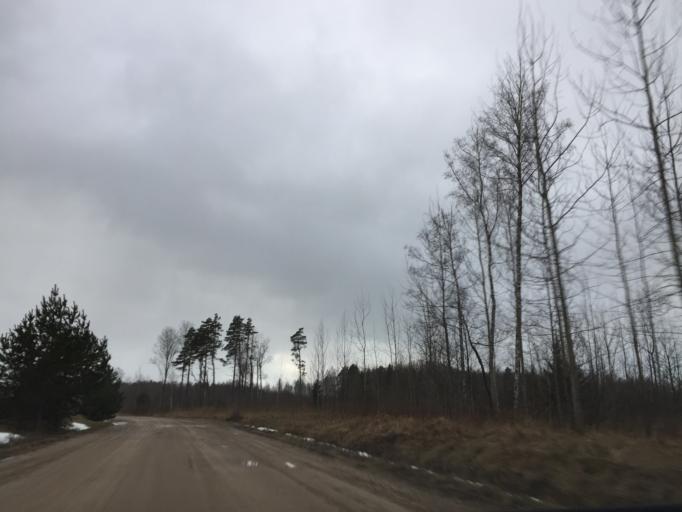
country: LV
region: Salacgrivas
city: Salacgriva
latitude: 57.6491
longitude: 24.4098
